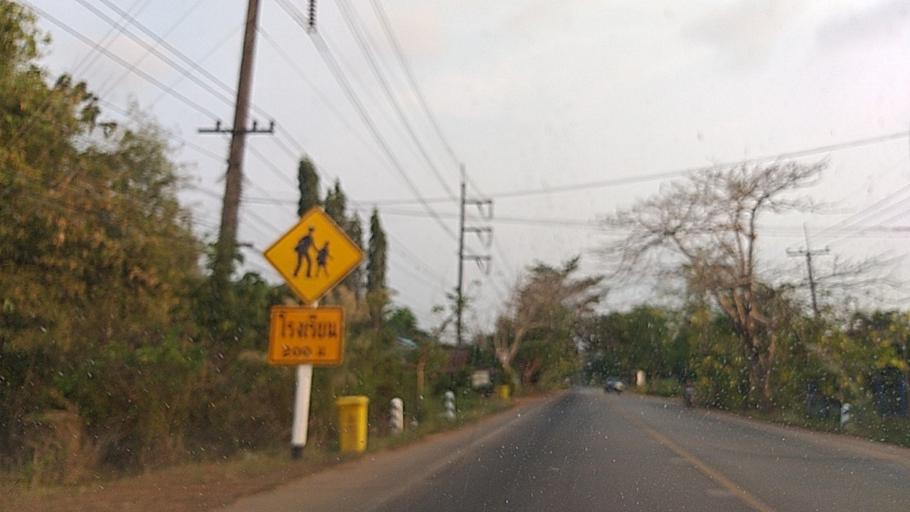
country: TH
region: Trat
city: Laem Ngop
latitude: 12.2311
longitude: 102.3049
